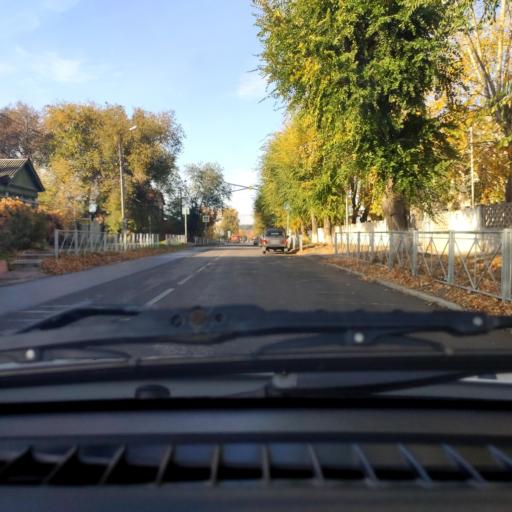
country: RU
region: Samara
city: Tol'yatti
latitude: 53.5348
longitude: 49.4055
